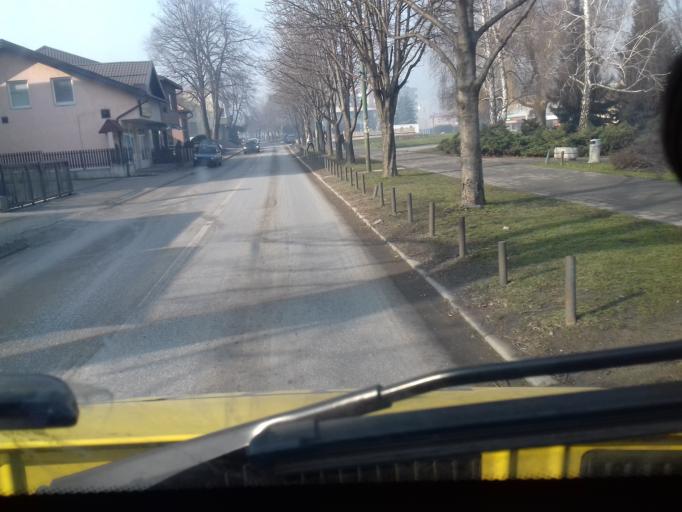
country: BA
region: Federation of Bosnia and Herzegovina
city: Visoko
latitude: 43.9937
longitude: 18.1754
